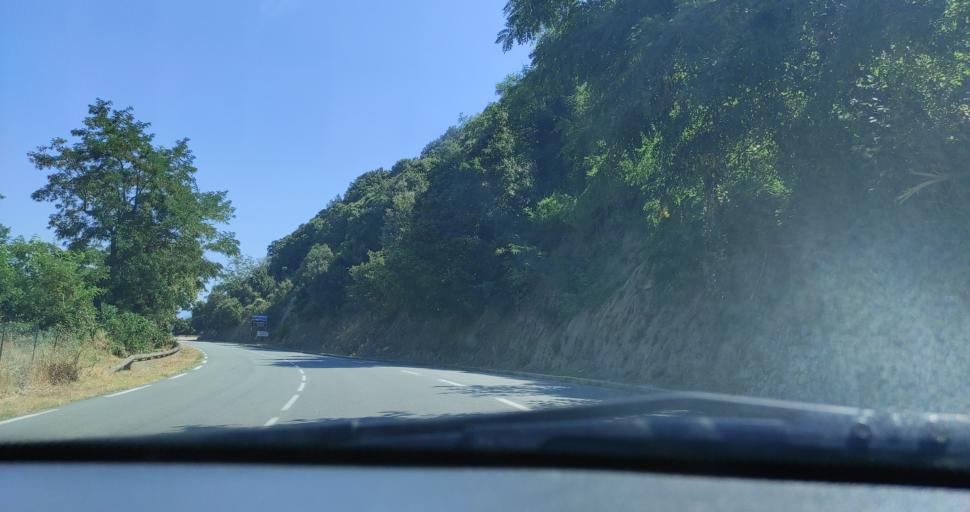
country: FR
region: Corsica
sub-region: Departement de la Corse-du-Sud
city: Sartene
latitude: 41.6166
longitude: 8.9590
